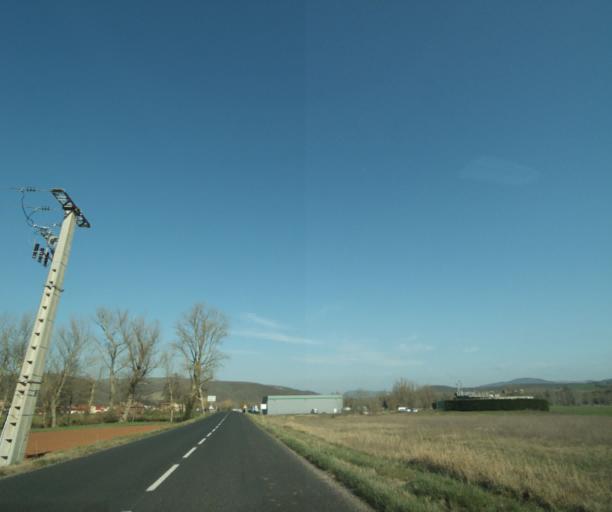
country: FR
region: Midi-Pyrenees
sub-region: Departement de l'Aveyron
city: Camares
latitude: 43.8810
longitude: 2.8201
